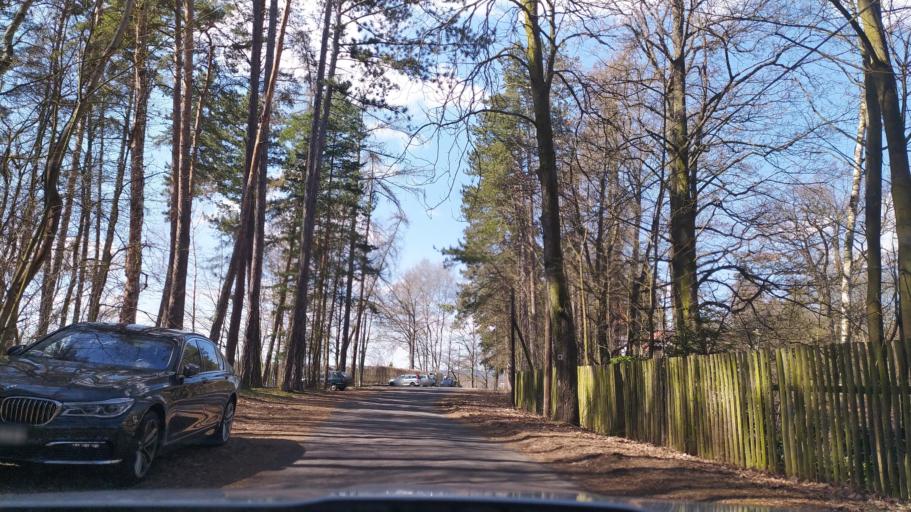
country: CZ
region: Karlovarsky
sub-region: Okres Cheb
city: Frantiskovy Lazne
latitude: 50.1116
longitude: 12.3318
